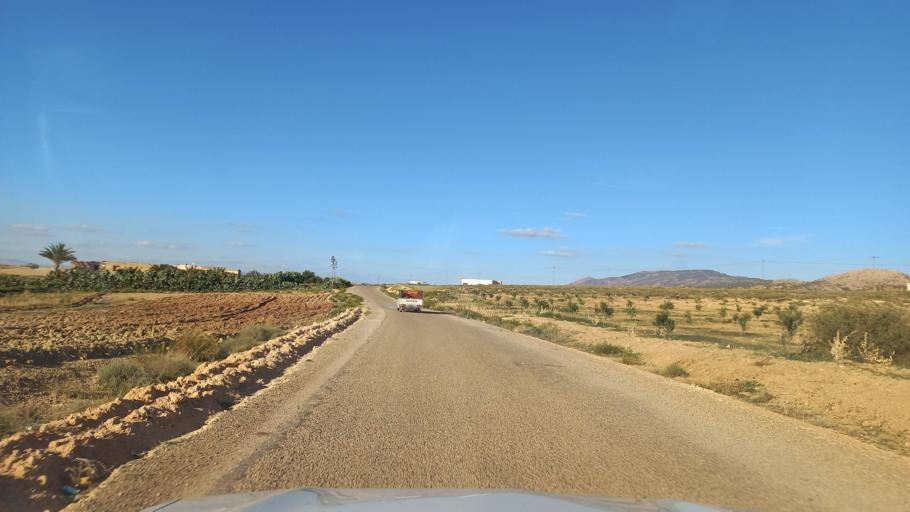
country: TN
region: Al Qasrayn
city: Sbiba
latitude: 35.3537
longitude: 9.1363
